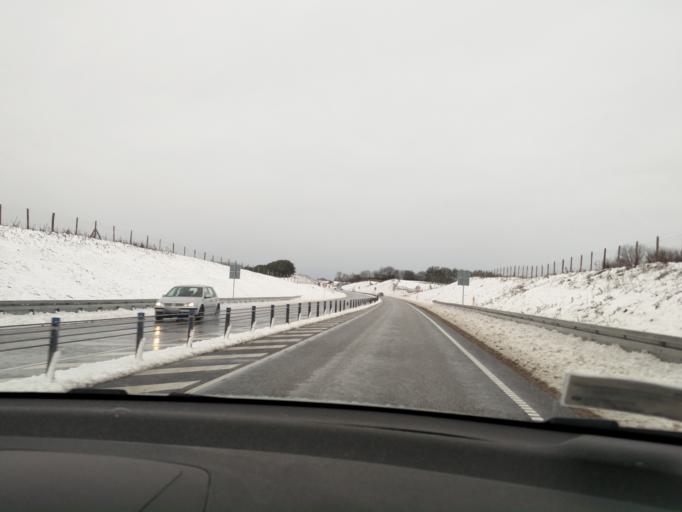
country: DK
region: Zealand
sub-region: Odsherred Kommune
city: Hojby
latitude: 55.8295
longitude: 11.5909
